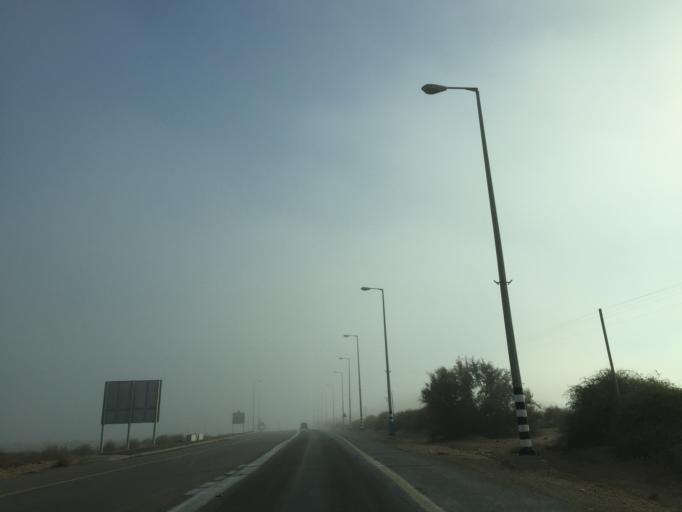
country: IL
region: Southern District
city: Yeroham
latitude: 30.9921
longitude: 34.9138
